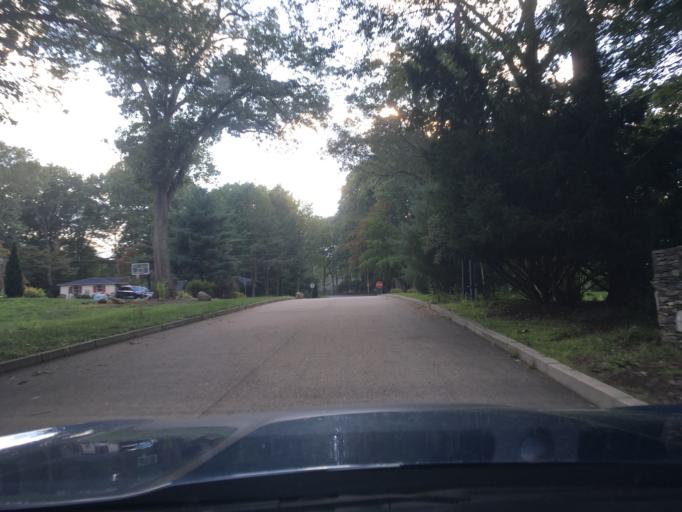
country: US
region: Rhode Island
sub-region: Kent County
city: East Greenwich
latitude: 41.6531
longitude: -71.4831
